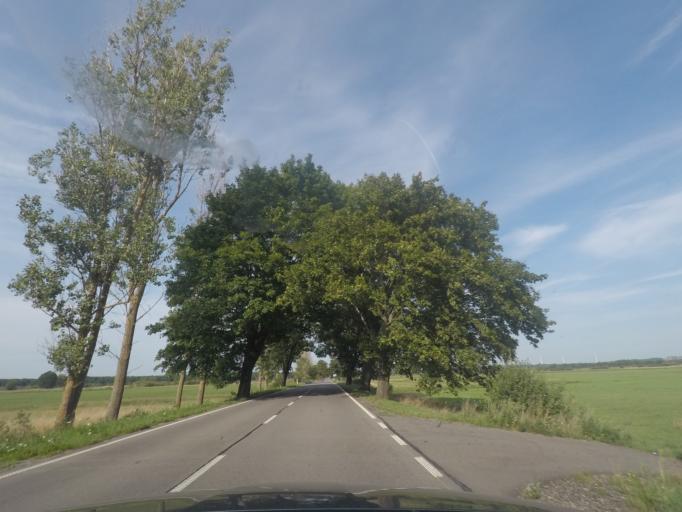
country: PL
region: Pomeranian Voivodeship
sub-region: Powiat leborski
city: Leba
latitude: 54.6507
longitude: 17.5566
